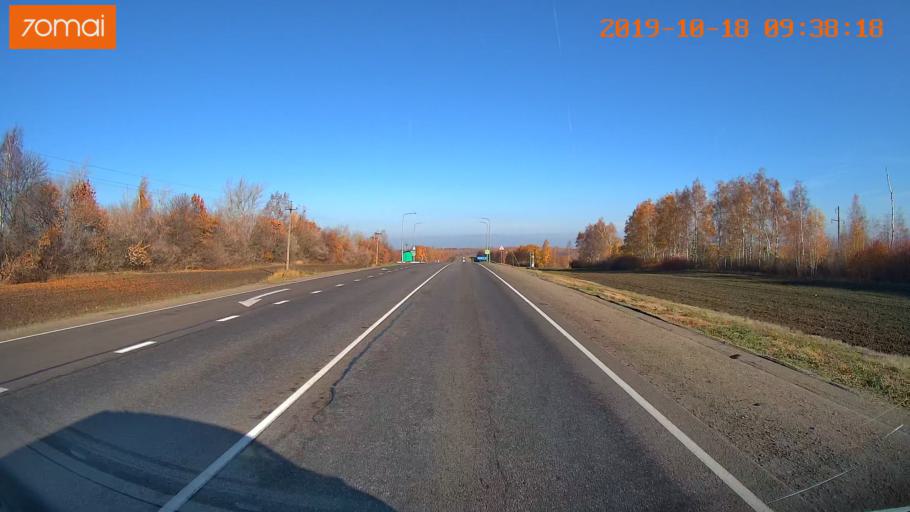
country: RU
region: Tula
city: Yefremov
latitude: 53.2360
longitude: 38.1376
